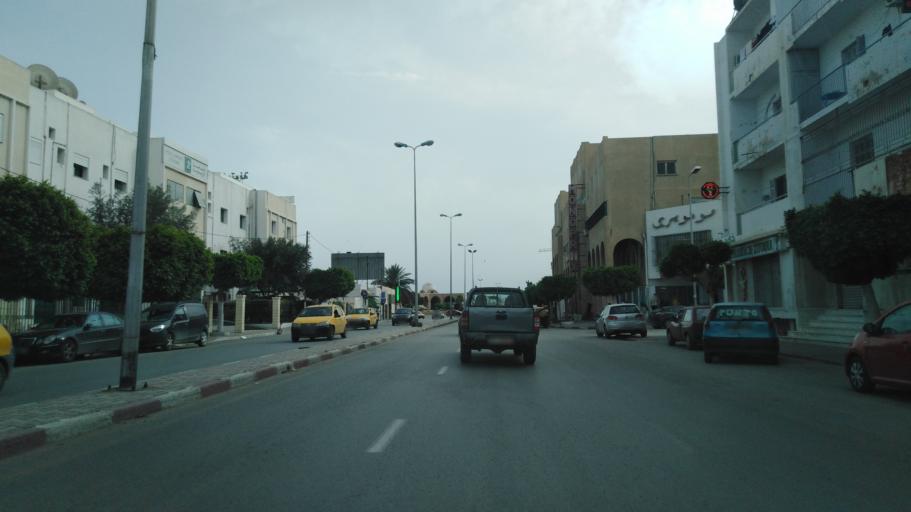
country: TN
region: Safaqis
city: Sfax
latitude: 34.7412
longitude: 10.7613
